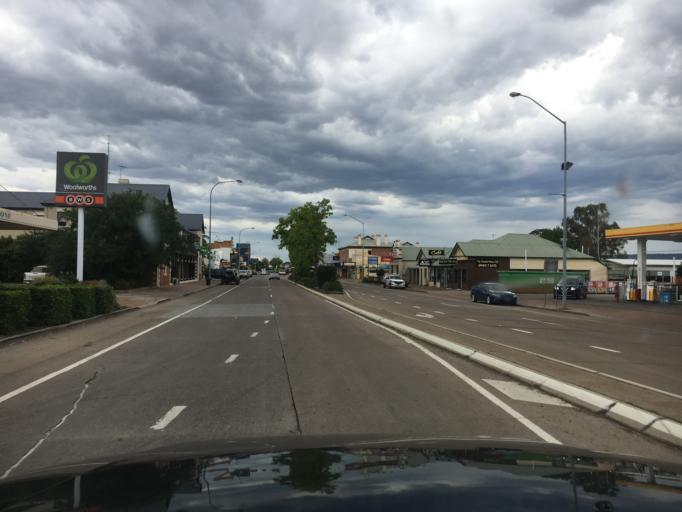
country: AU
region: New South Wales
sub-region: Muswellbrook
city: Muswellbrook
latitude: -32.0468
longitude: 150.8683
